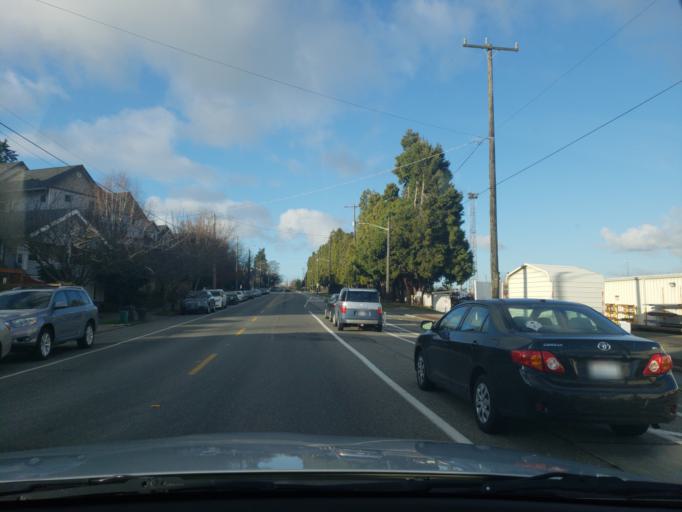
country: US
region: Washington
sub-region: King County
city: Seattle
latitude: 47.6522
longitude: -122.3833
